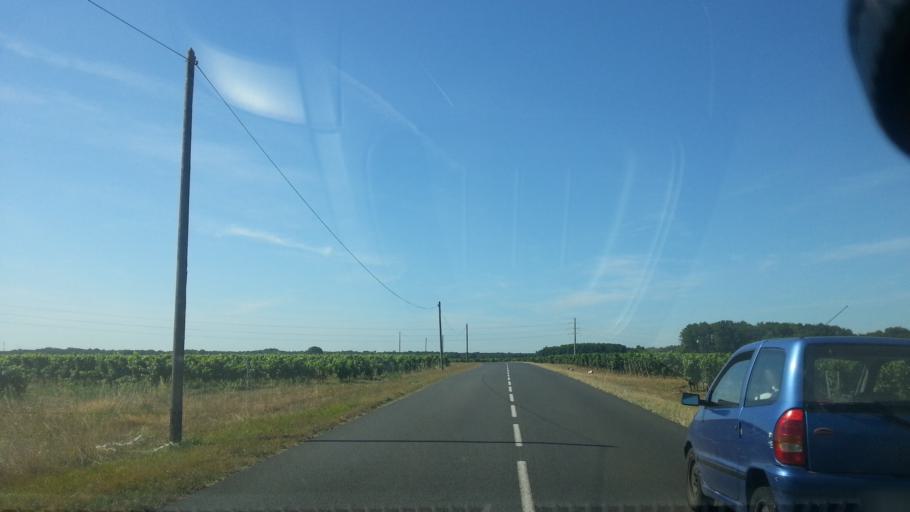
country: FR
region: Aquitaine
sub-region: Departement de la Gironde
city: Podensac
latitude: 44.6399
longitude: -0.3623
